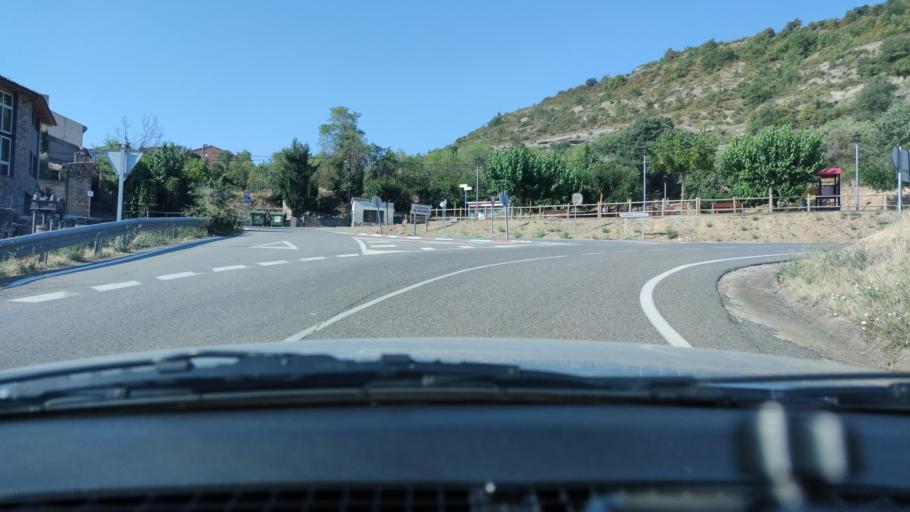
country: ES
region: Catalonia
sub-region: Provincia de Lleida
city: Llimiana
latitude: 42.0933
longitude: 0.8767
